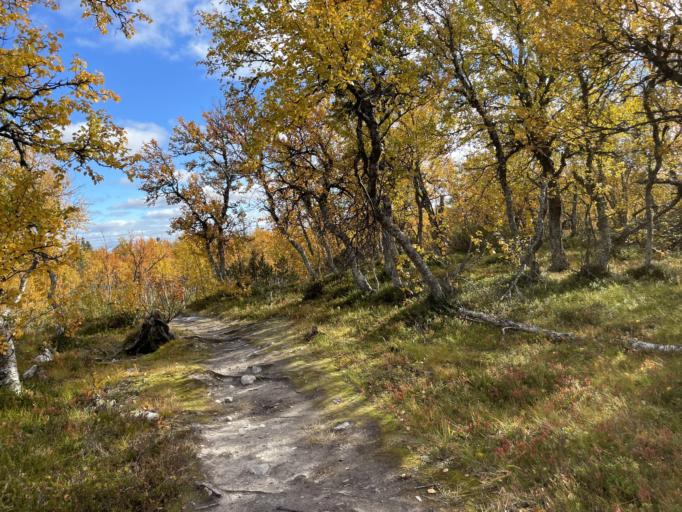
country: SE
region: Jaemtland
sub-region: Are Kommun
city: Are
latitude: 62.6910
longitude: 12.9100
